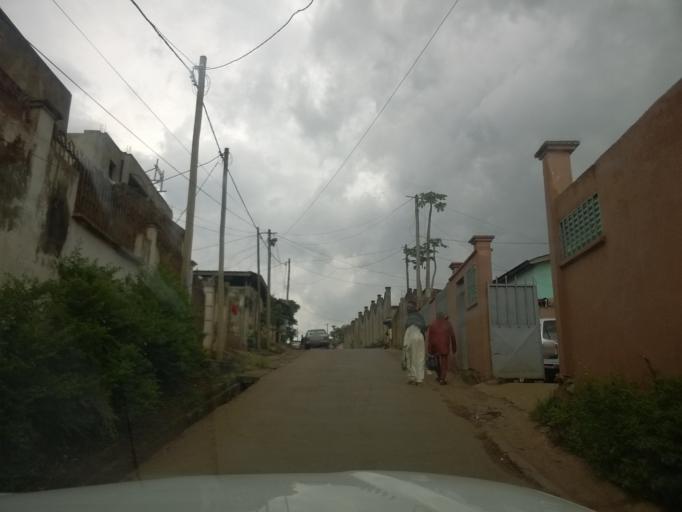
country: CM
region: Centre
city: Yaounde
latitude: 3.9117
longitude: 11.5250
